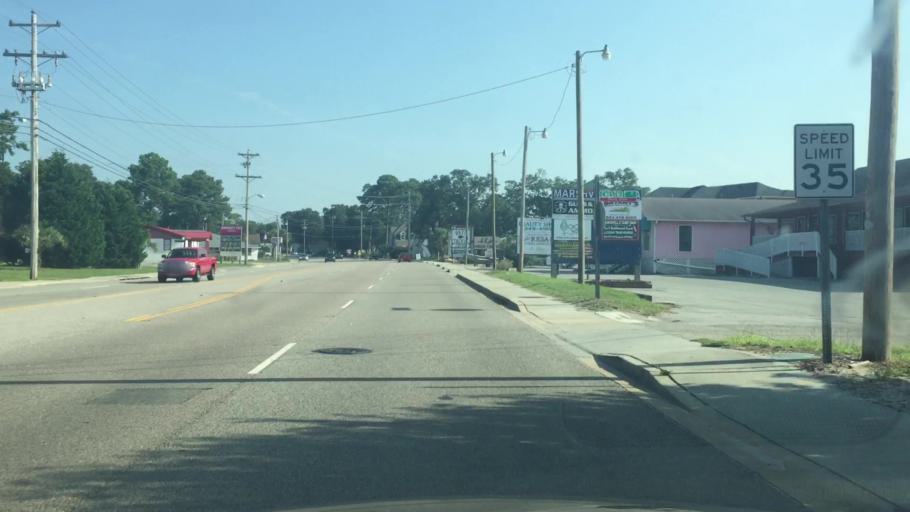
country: US
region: South Carolina
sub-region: Horry County
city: North Myrtle Beach
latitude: 33.8354
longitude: -78.6445
